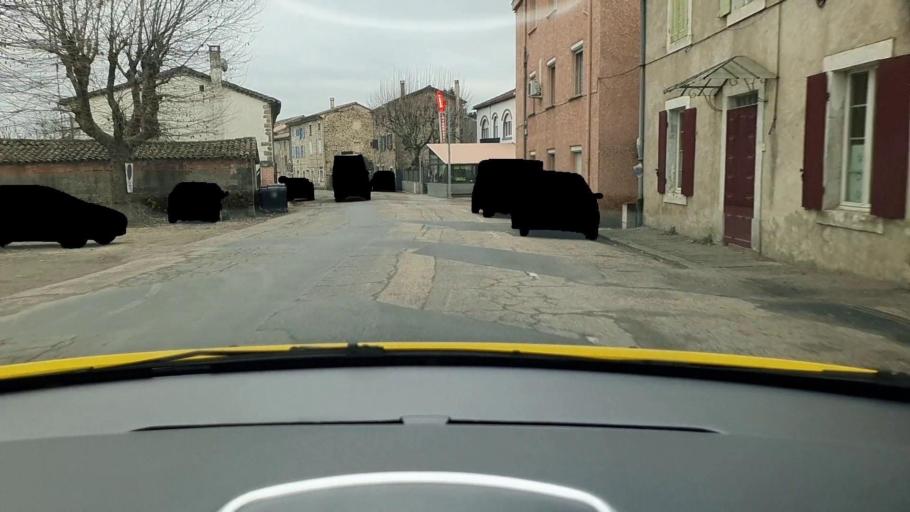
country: FR
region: Languedoc-Roussillon
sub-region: Departement du Gard
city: Laval-Pradel
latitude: 44.2323
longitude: 4.0571
